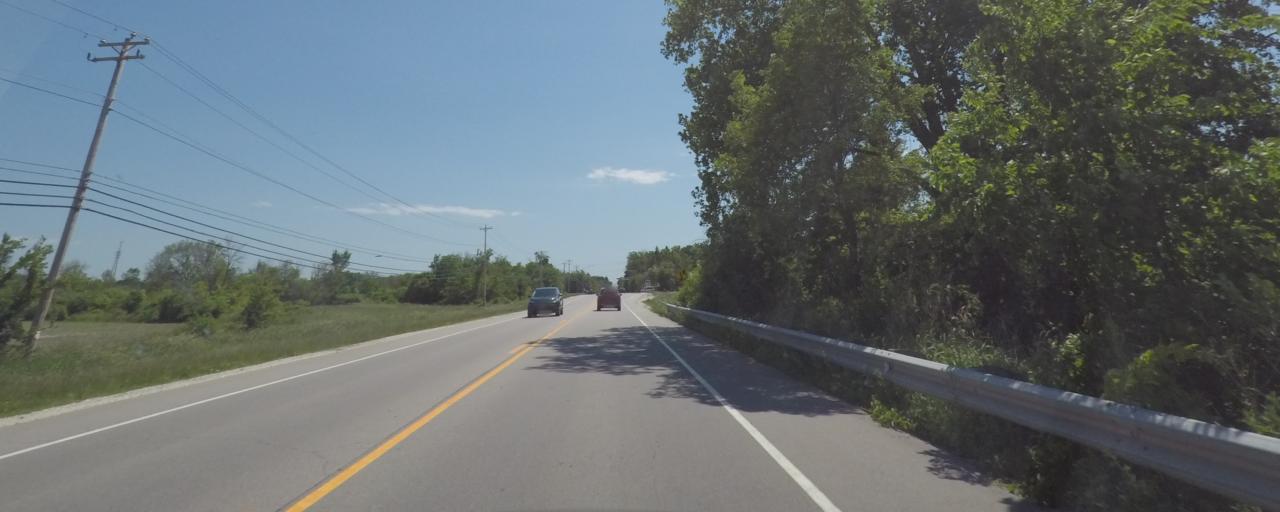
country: US
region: Wisconsin
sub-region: Waukesha County
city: New Berlin
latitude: 42.9834
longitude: -88.1283
